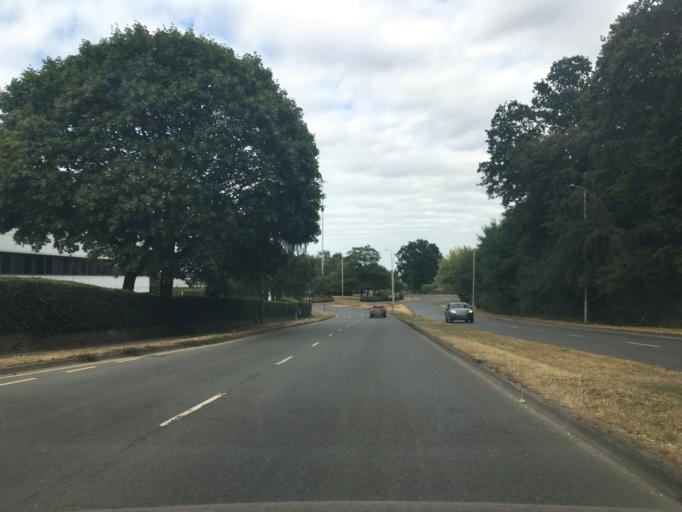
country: GB
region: England
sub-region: Hertfordshire
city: Hemel Hempstead
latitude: 51.7661
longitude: -0.4460
